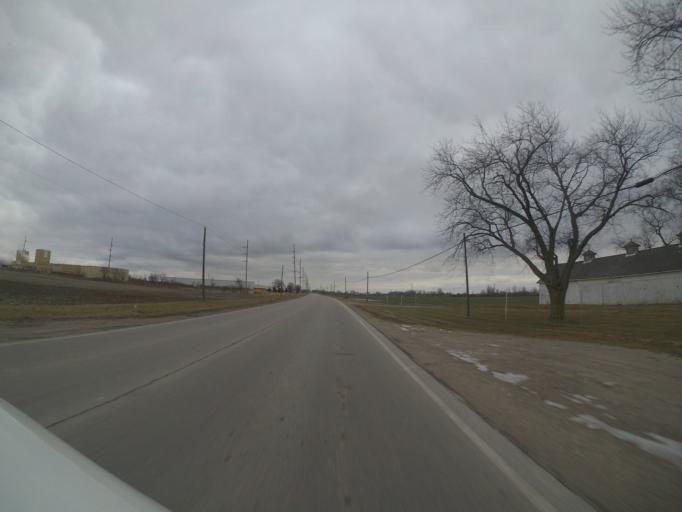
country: US
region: Ohio
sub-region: Wood County
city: Walbridge
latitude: 41.5991
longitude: -83.5128
